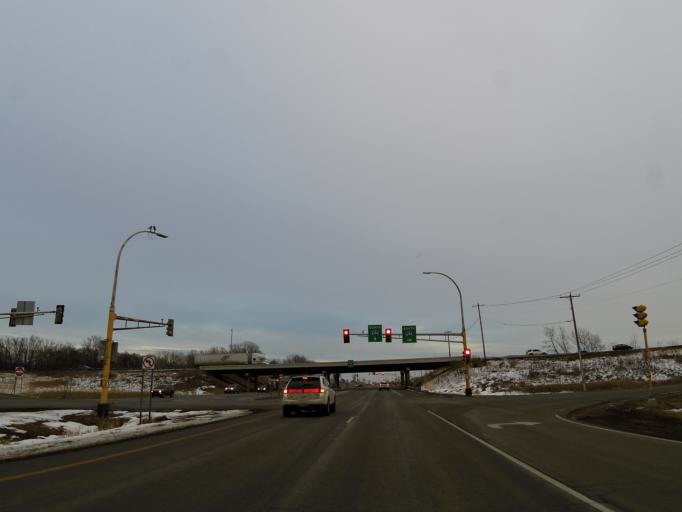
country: US
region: Minnesota
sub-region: Ramsey County
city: North Saint Paul
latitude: 44.9976
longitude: -92.9612
